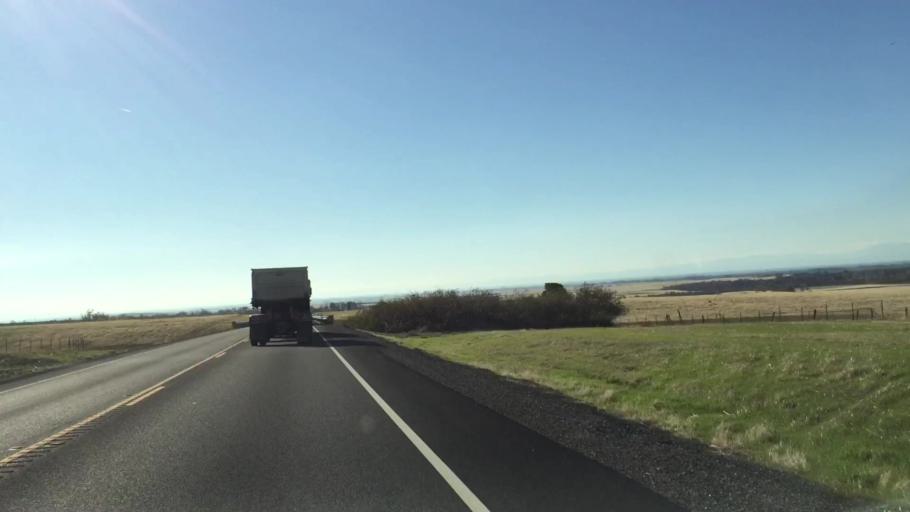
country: US
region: California
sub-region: Butte County
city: Thermalito
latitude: 39.6173
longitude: -121.6020
